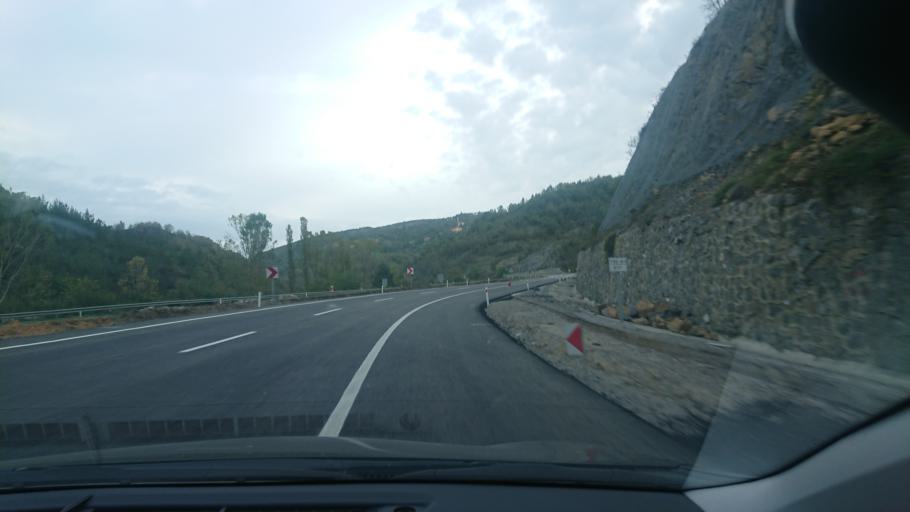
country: TR
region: Zonguldak
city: Beycuma
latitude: 41.3970
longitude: 31.9361
